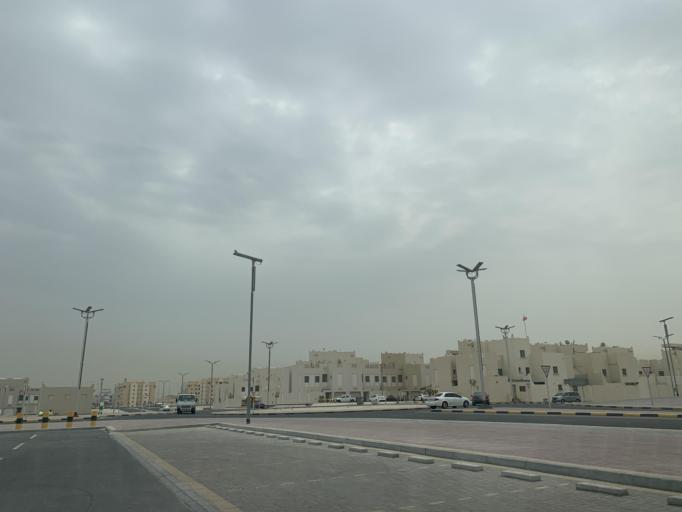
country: BH
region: Northern
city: Madinat `Isa
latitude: 26.1774
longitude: 50.5169
